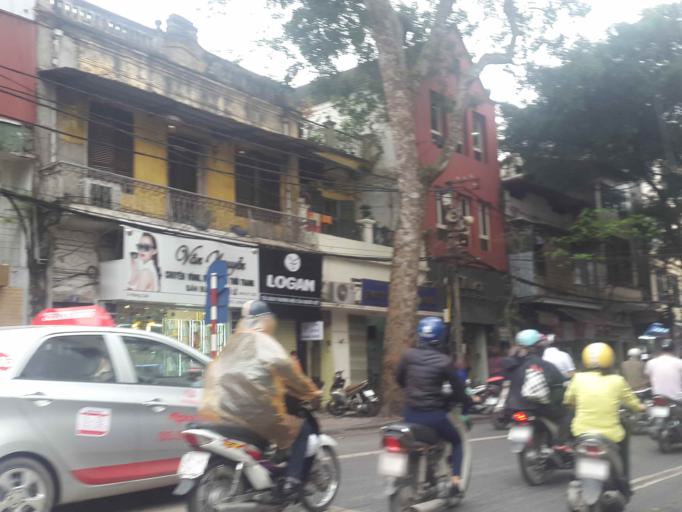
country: VN
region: Ha Noi
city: Hoan Kiem
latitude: 21.0397
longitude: 105.8471
